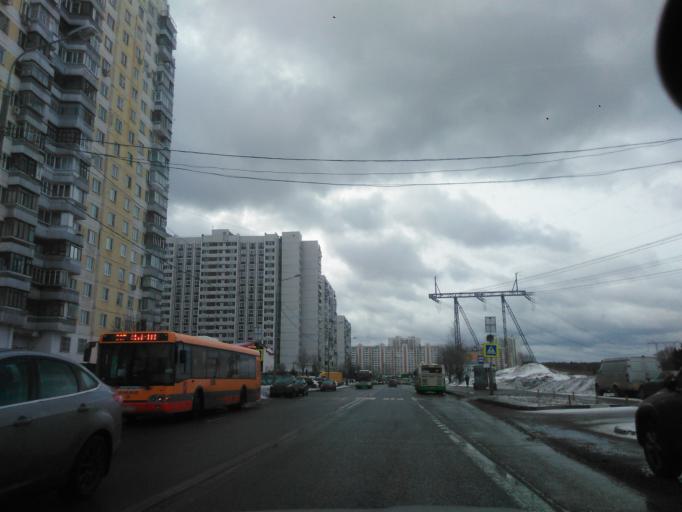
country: RU
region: Moskovskaya
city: Krasnogorsk
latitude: 55.8540
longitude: 37.3424
